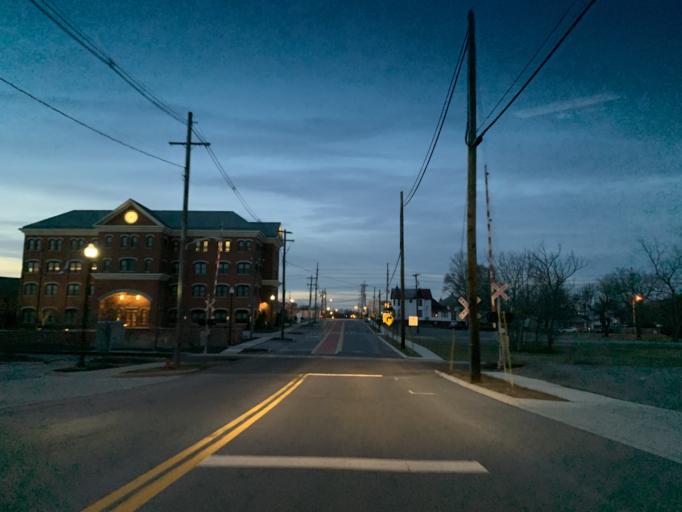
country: US
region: West Virginia
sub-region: Jefferson County
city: Charles Town
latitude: 39.2908
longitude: -77.8609
